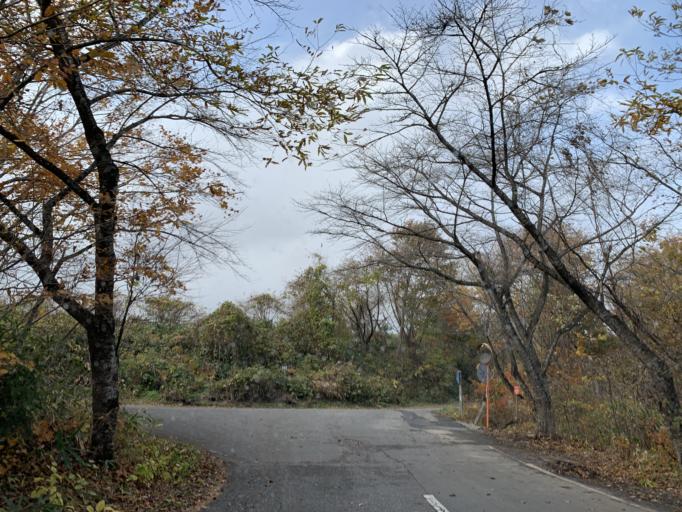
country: JP
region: Iwate
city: Mizusawa
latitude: 39.0430
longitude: 141.0760
